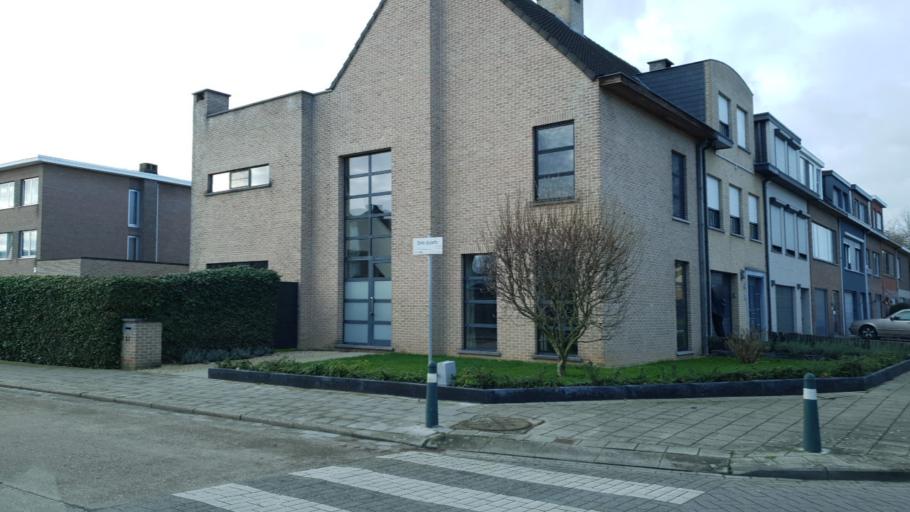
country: BE
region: Flanders
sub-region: Provincie Antwerpen
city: Lier
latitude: 51.1485
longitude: 4.5738
